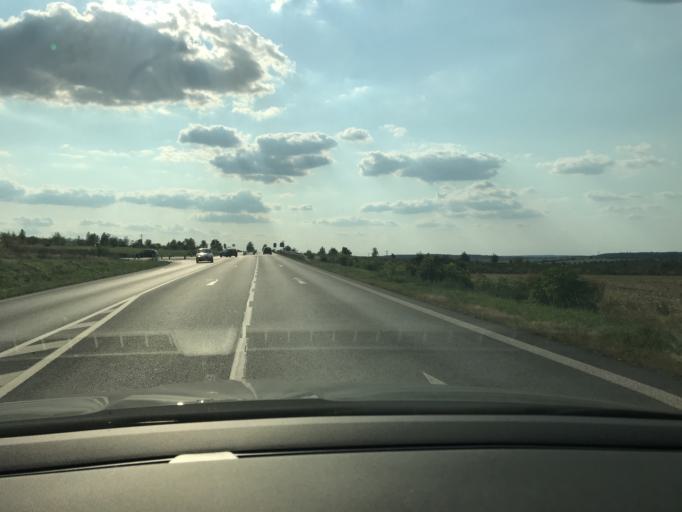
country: CZ
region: Central Bohemia
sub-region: Okres Kladno
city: Slany
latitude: 50.2343
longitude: 14.0581
